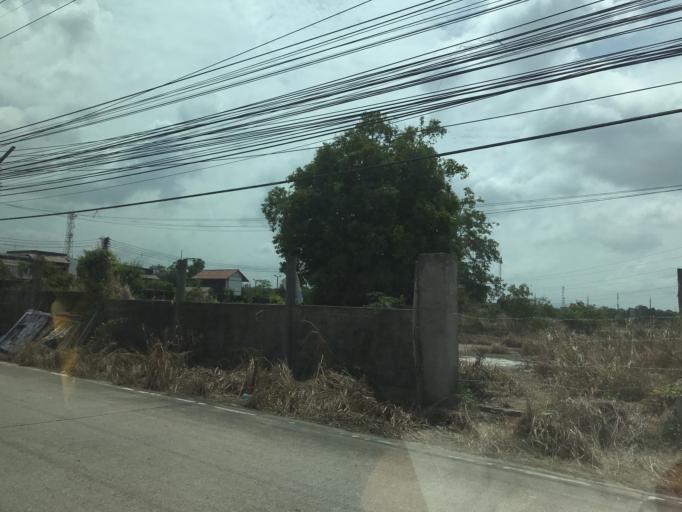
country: TH
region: Chon Buri
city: Si Racha
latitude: 13.1514
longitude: 100.9827
